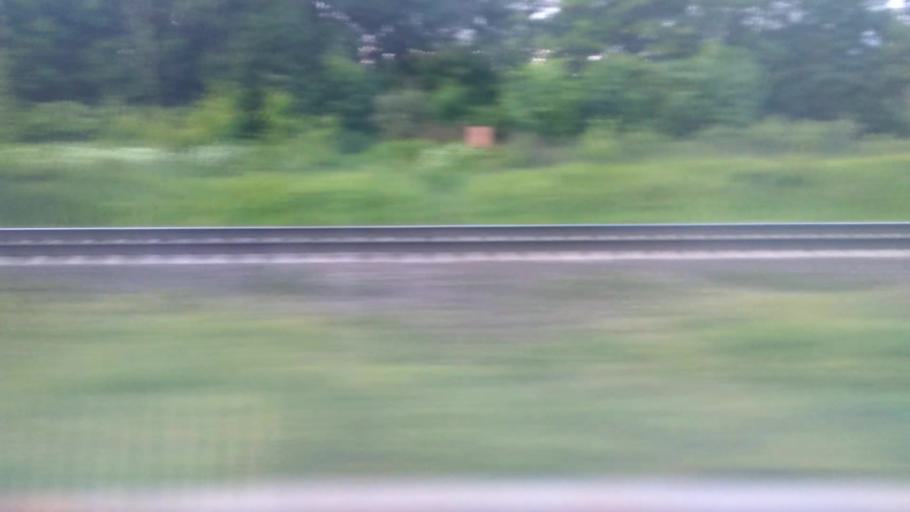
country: RU
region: Moskovskaya
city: Vostryakovo
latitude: 55.4044
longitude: 37.7983
